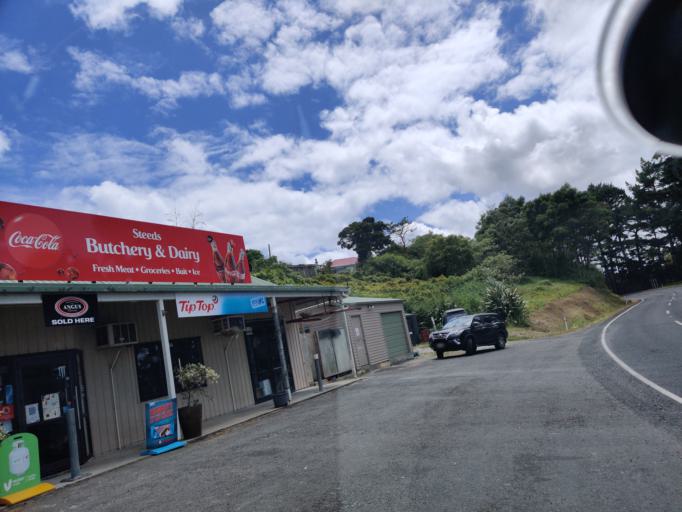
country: NZ
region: Northland
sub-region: Far North District
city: Kaitaia
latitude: -34.9515
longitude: 173.1863
